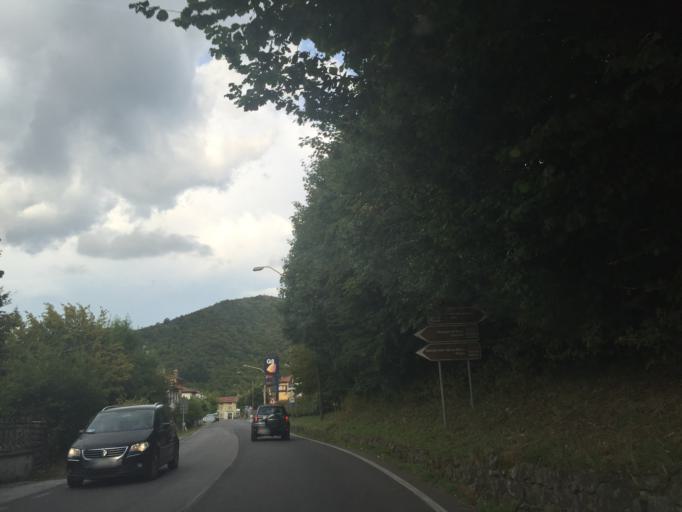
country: IT
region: Tuscany
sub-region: Provincia di Pistoia
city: Campo Tizzoro
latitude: 44.0377
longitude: 10.8790
